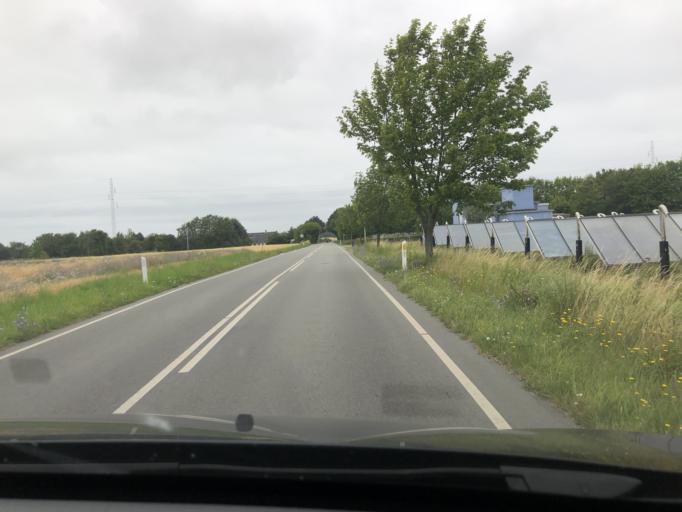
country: DK
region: South Denmark
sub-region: AEro Kommune
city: Marstal
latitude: 54.8528
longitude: 10.4982
